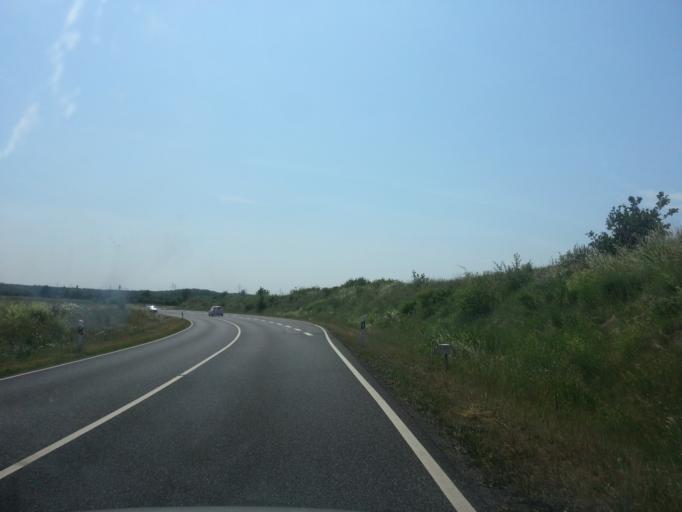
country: DE
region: Hesse
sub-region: Regierungsbezirk Darmstadt
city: Dietzenbach
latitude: 50.0016
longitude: 8.7393
